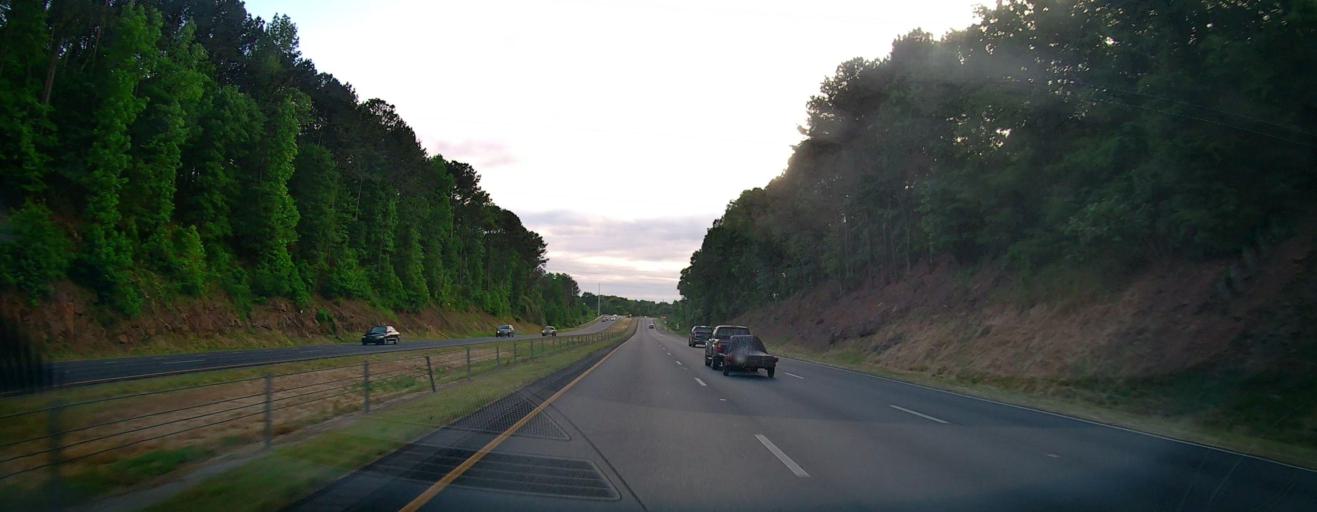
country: US
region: Georgia
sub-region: Clarke County
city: Athens
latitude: 33.9733
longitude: -83.3950
